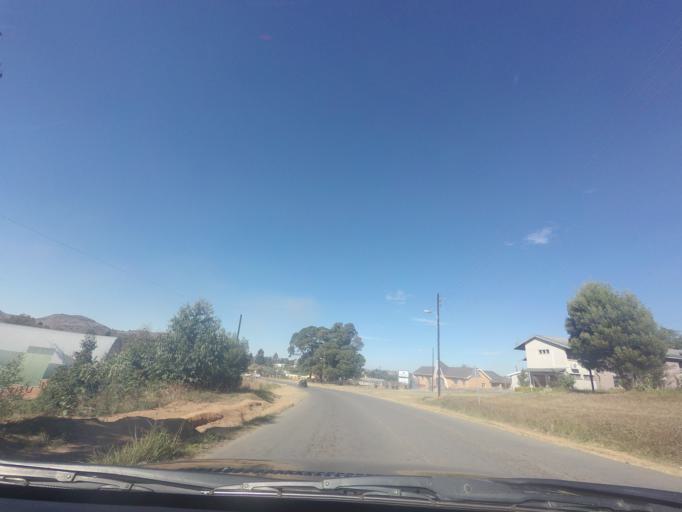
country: SZ
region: Hhohho
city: Mbabane
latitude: -26.3121
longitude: 31.1235
